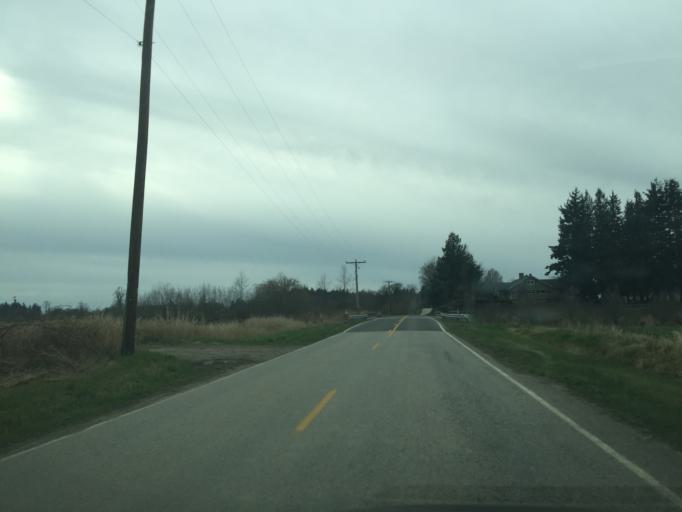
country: US
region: Washington
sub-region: Whatcom County
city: Nooksack
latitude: 48.9784
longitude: -122.3174
